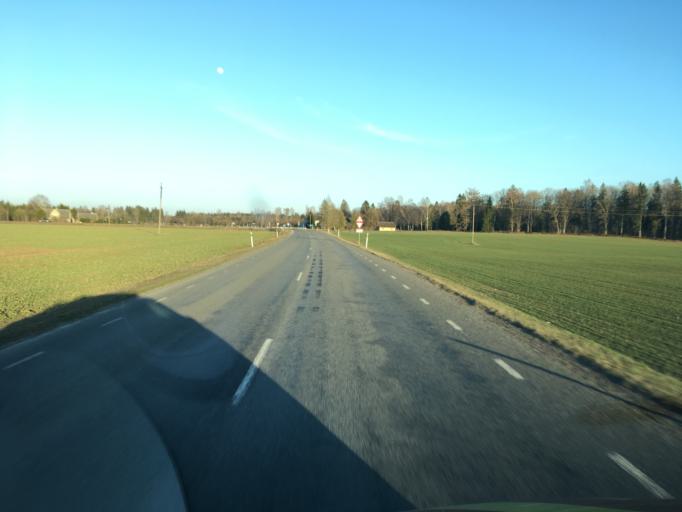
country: EE
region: Raplamaa
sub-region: Kehtna vald
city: Kehtna
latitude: 59.0567
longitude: 24.9459
